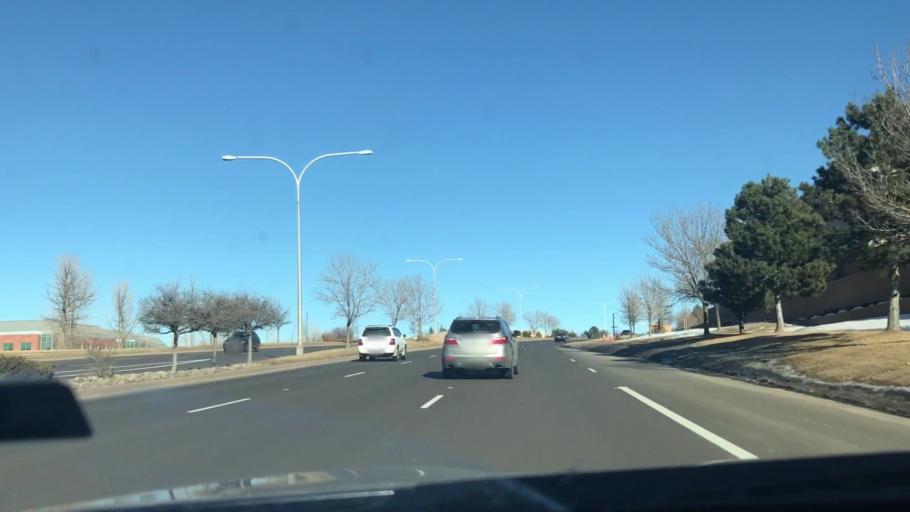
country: US
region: Colorado
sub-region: El Paso County
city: Air Force Academy
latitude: 38.9659
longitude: -104.7881
